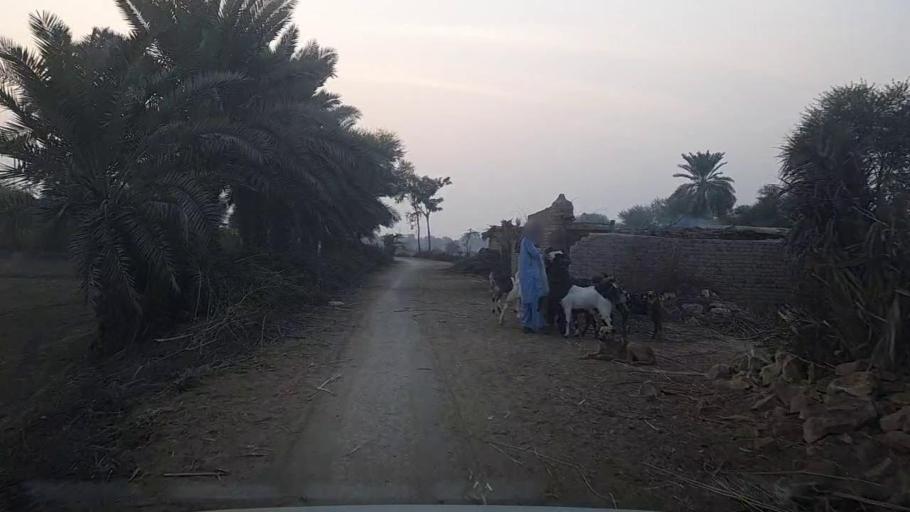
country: PK
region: Sindh
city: Kot Diji
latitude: 27.3376
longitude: 68.6404
